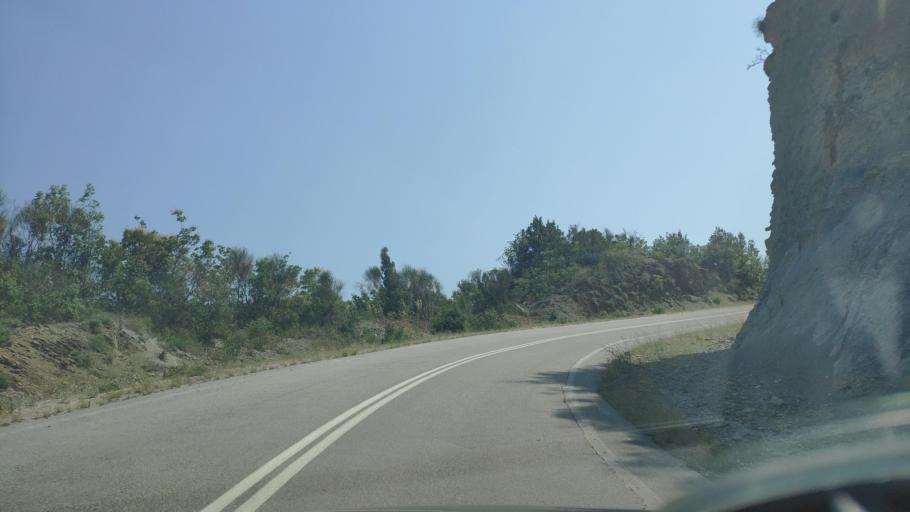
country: GR
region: Epirus
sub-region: Nomos Artas
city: Ano Kalentini
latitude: 39.2205
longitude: 21.1501
